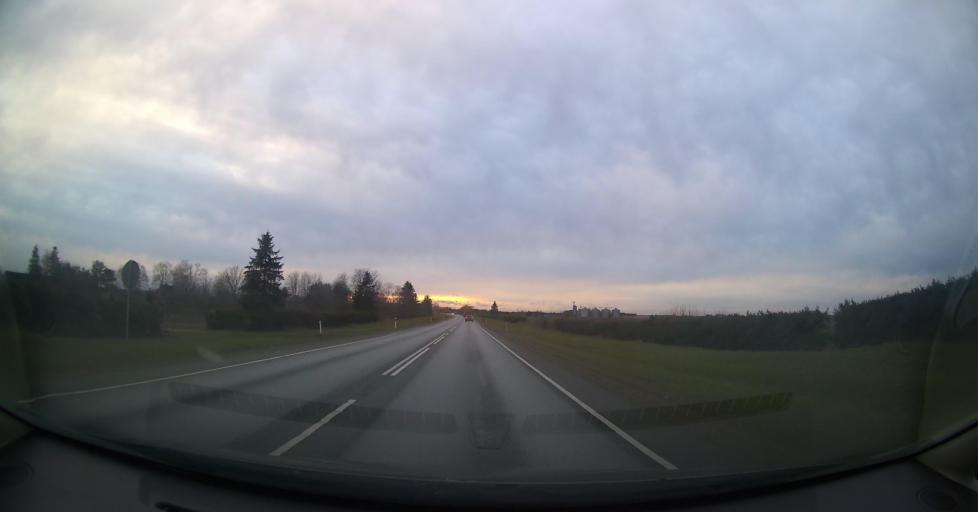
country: EE
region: Ida-Virumaa
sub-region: Kohtla-Nomme vald
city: Kohtla-Nomme
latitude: 59.4103
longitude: 27.1214
